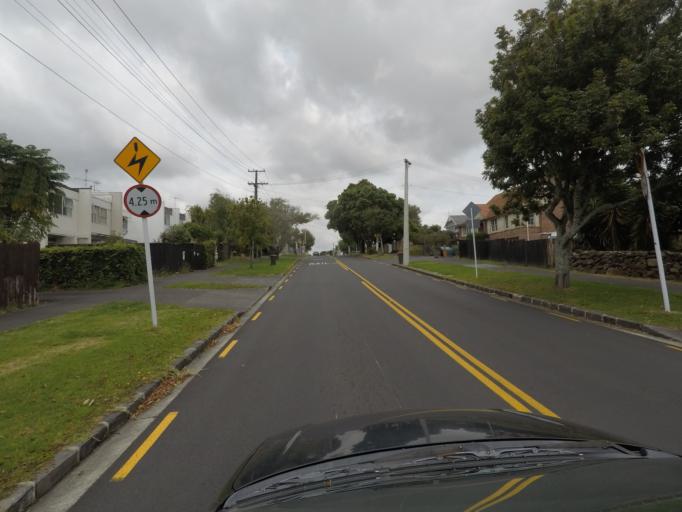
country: NZ
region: Auckland
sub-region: Auckland
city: Auckland
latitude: -36.8765
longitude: 174.7238
